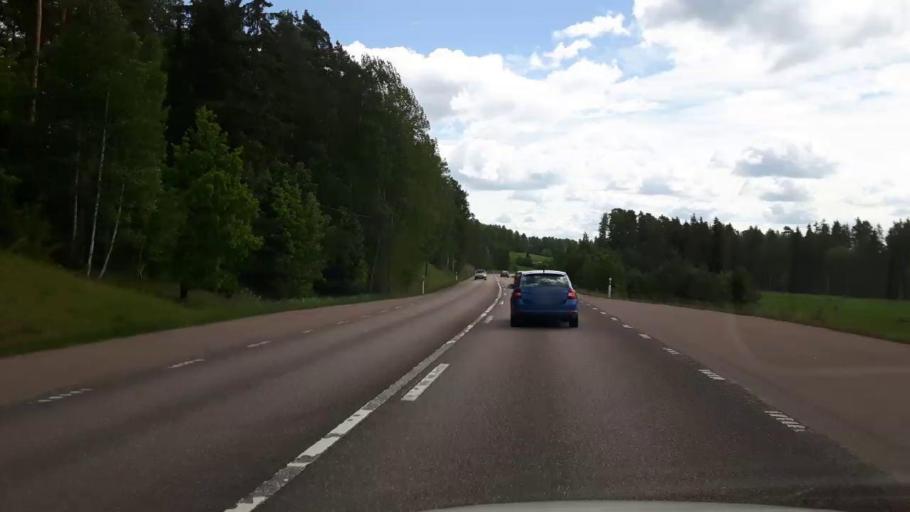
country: SE
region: Dalarna
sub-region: Saters Kommun
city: Saeter
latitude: 60.4353
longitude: 15.8251
